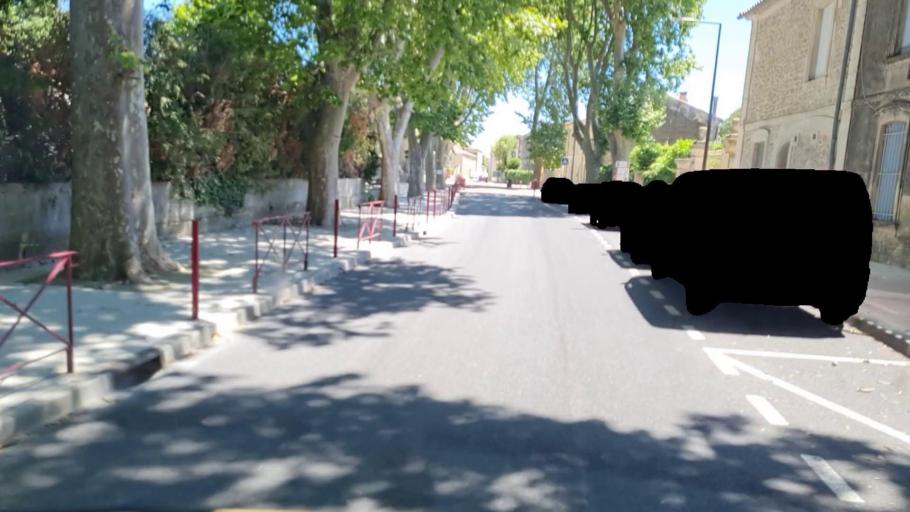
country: FR
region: Languedoc-Roussillon
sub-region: Departement du Gard
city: Le Cailar
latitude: 43.6780
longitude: 4.2356
